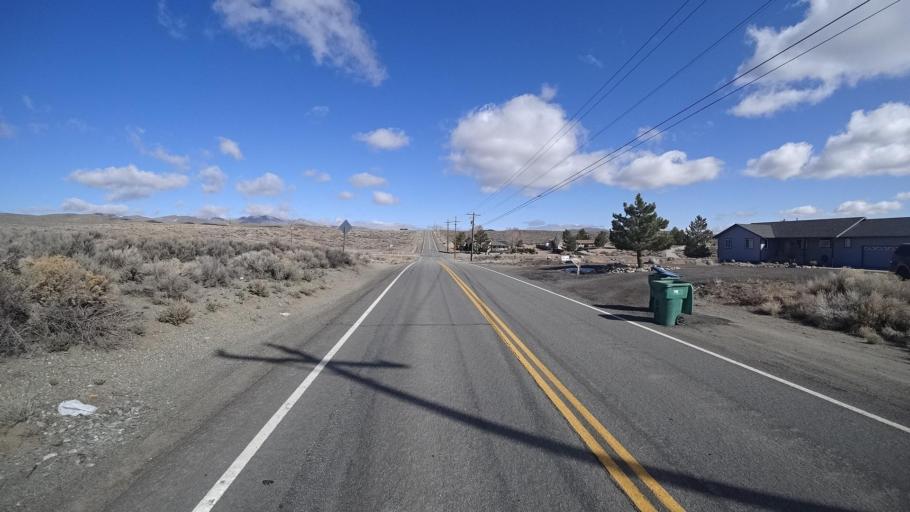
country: US
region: Nevada
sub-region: Washoe County
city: Cold Springs
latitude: 39.6662
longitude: -119.9224
